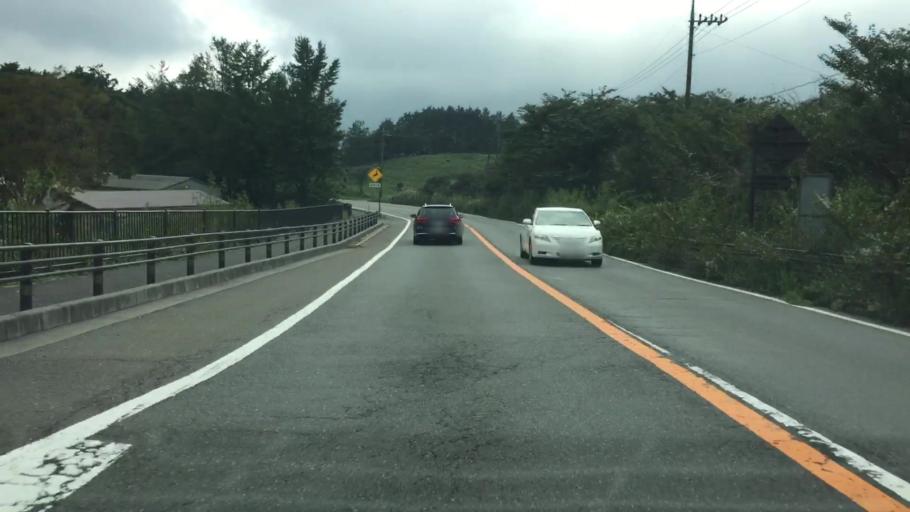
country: JP
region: Yamanashi
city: Fujikawaguchiko
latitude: 35.4042
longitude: 138.5834
